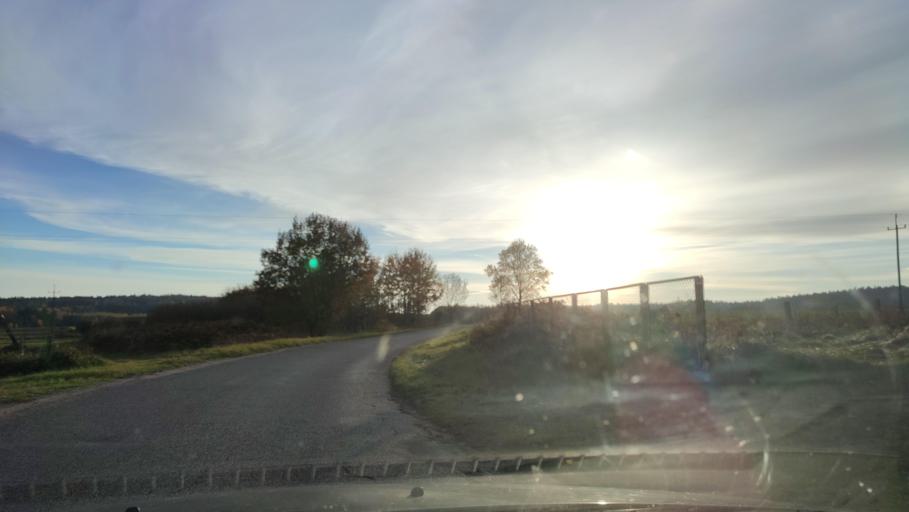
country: PL
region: Masovian Voivodeship
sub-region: Powiat przasnyski
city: Chorzele
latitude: 53.3381
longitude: 20.7517
